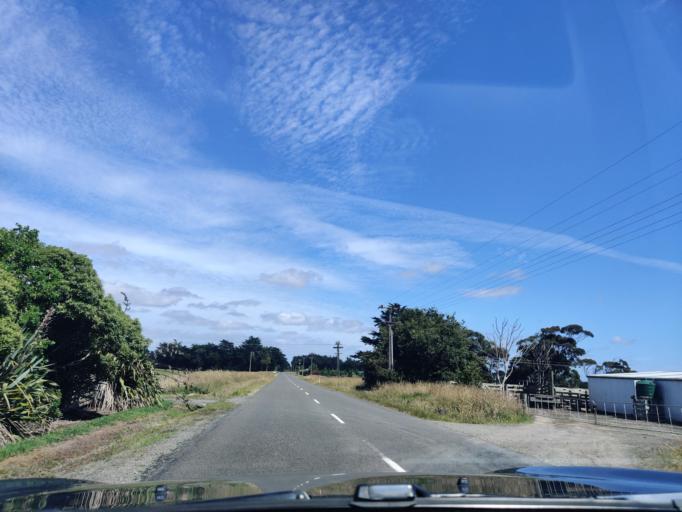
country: NZ
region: Manawatu-Wanganui
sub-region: Rangitikei District
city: Bulls
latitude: -40.1910
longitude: 175.4647
